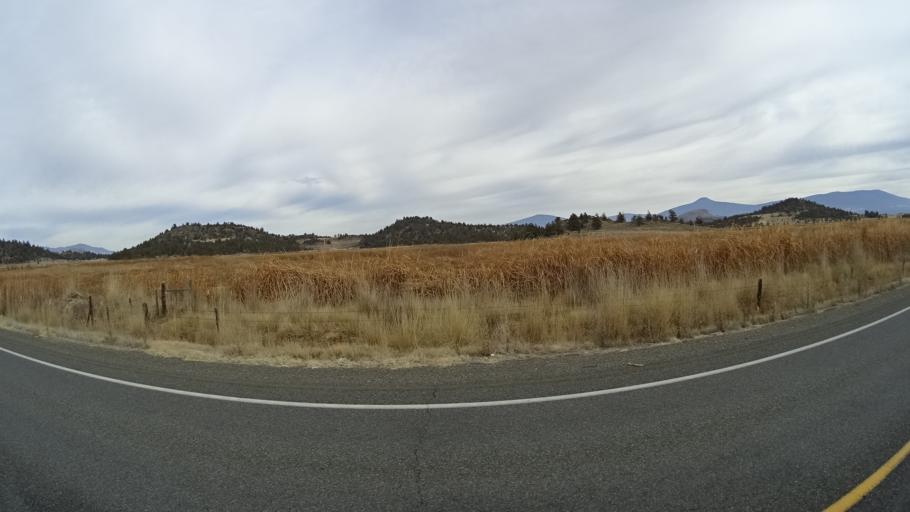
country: US
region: California
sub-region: Siskiyou County
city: Montague
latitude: 41.6447
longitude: -122.4906
